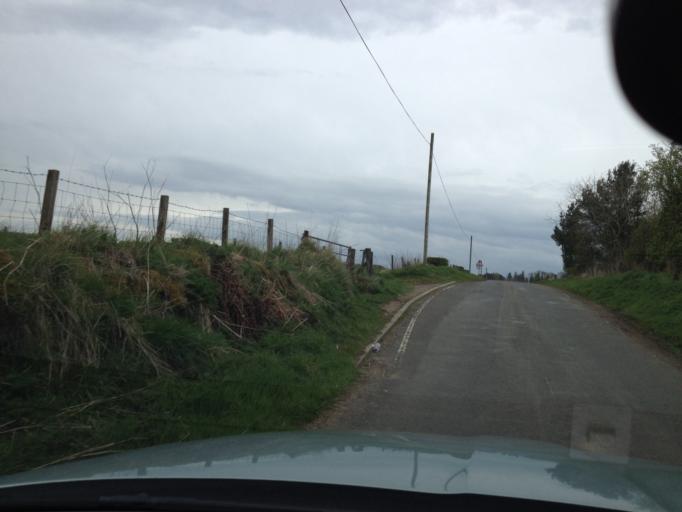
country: GB
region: Scotland
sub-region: West Lothian
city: Linlithgow
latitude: 55.9375
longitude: -3.5821
